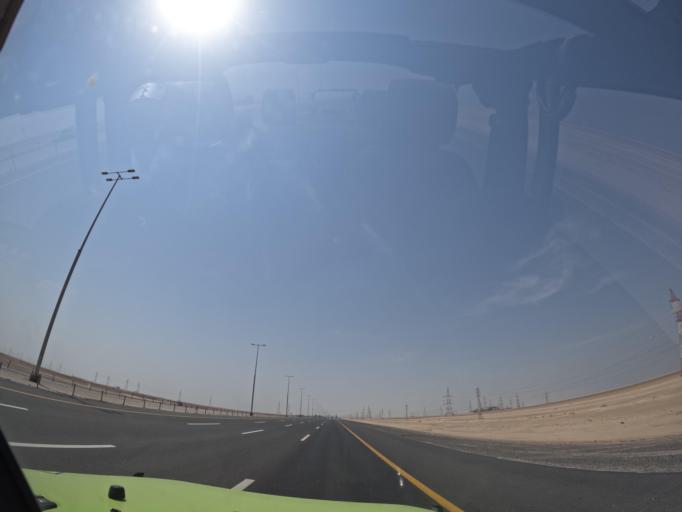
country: AE
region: Abu Dhabi
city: Abu Dhabi
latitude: 24.1565
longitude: 54.3174
